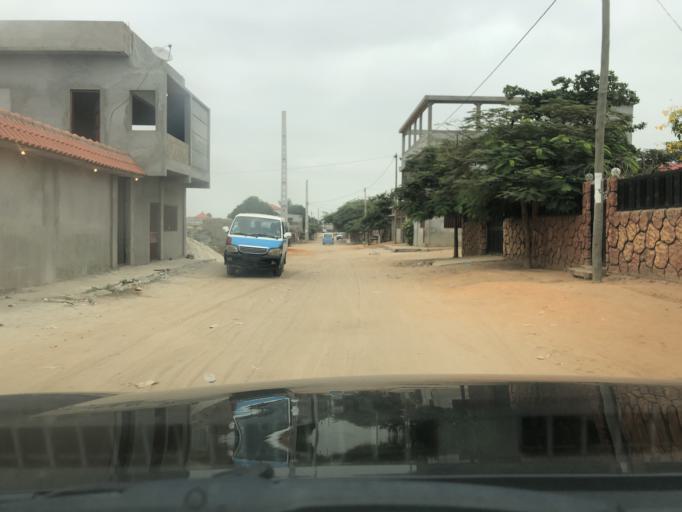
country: AO
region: Luanda
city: Luanda
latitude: -8.9379
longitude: 13.2285
